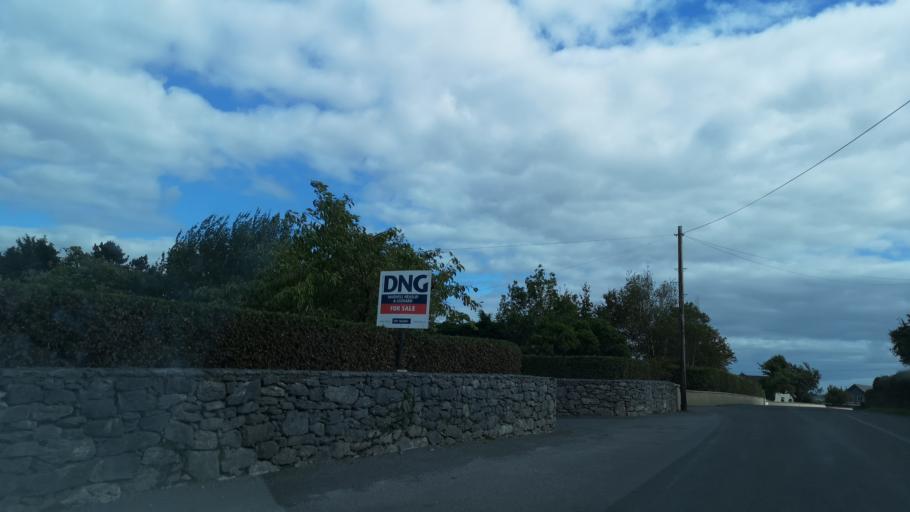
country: IE
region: Connaught
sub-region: County Galway
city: Moycullen
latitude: 53.3483
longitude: -9.1728
